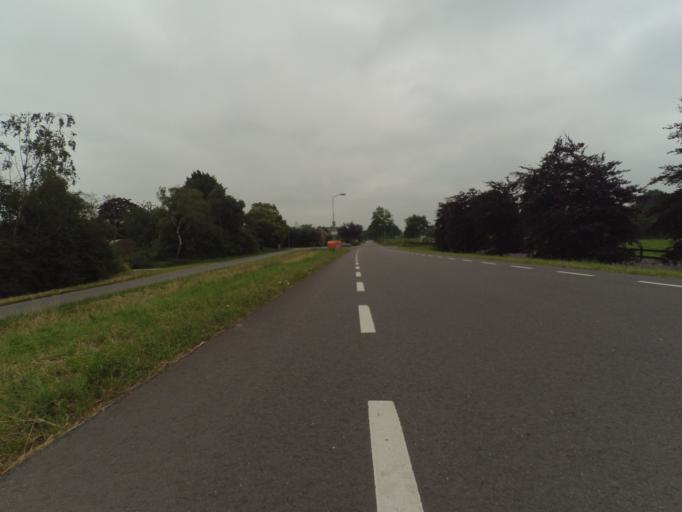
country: NL
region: Gelderland
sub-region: Gemeente Barneveld
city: Kootwijkerbroek
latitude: 52.1710
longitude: 5.6396
